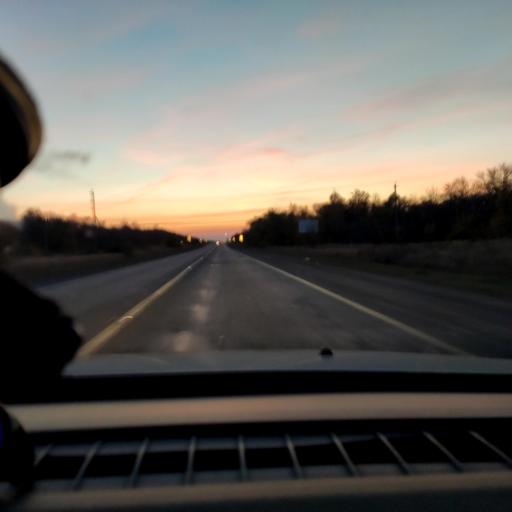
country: RU
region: Samara
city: Chapayevsk
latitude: 52.9968
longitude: 49.7819
